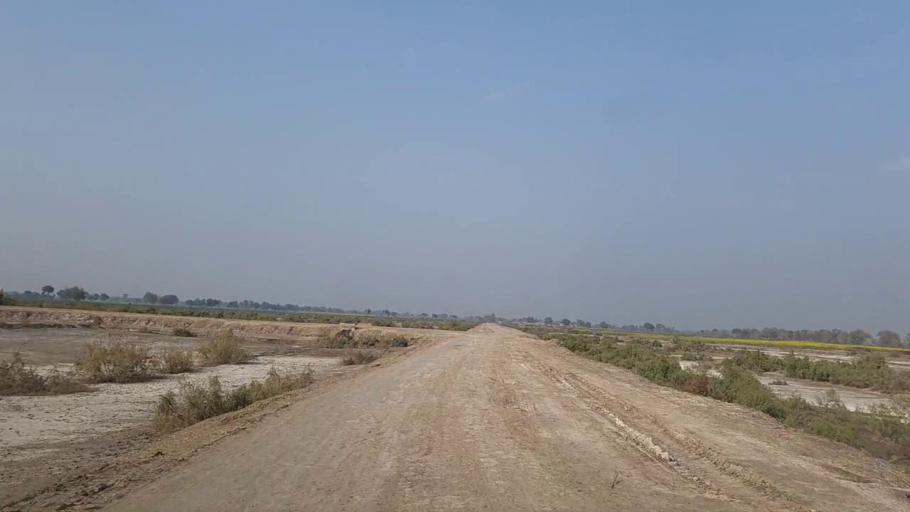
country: PK
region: Sindh
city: Nawabshah
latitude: 26.3423
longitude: 68.4739
